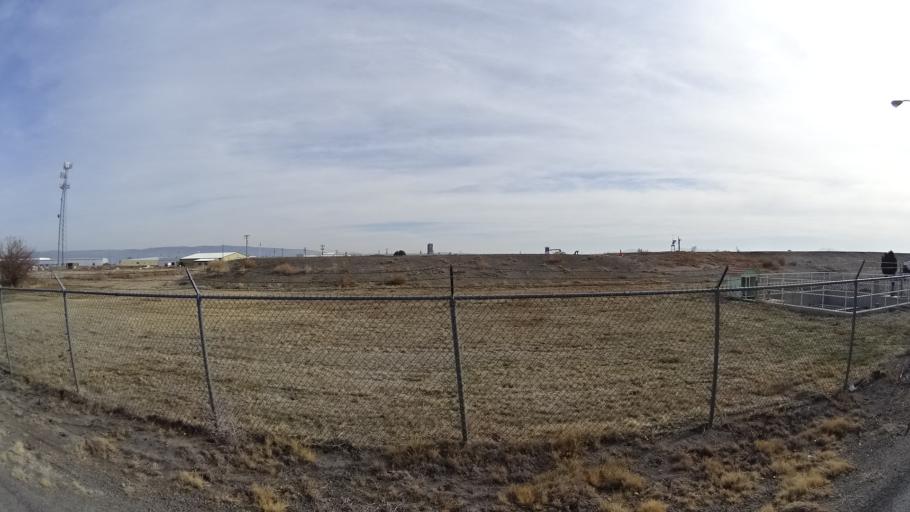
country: US
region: California
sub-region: Siskiyou County
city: Tulelake
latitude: 41.9486
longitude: -121.4715
